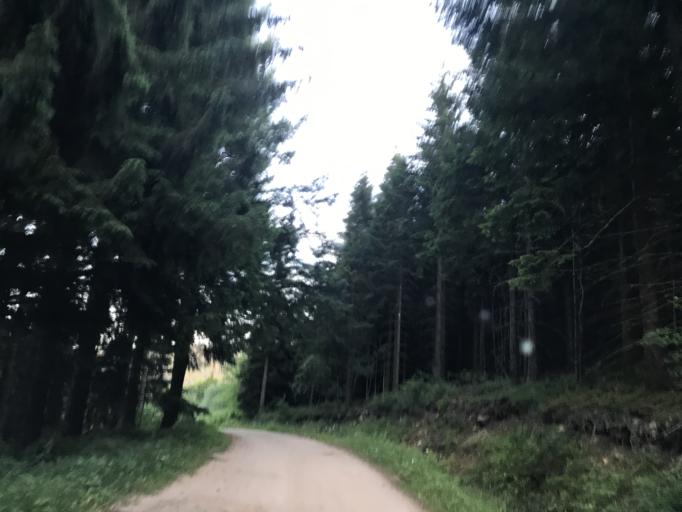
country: FR
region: Rhone-Alpes
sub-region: Departement de la Loire
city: Noiretable
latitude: 45.8065
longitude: 3.7045
